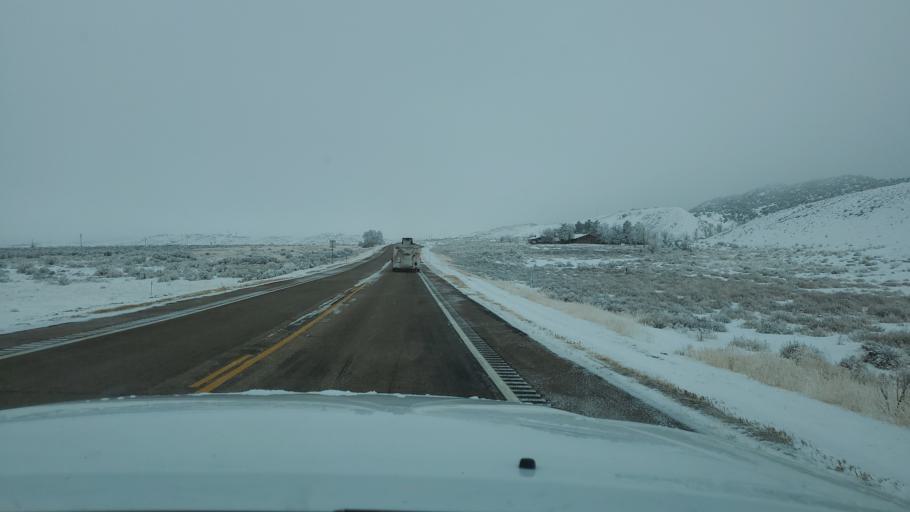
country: US
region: Colorado
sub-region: Rio Blanco County
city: Rangely
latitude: 40.2428
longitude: -108.9685
